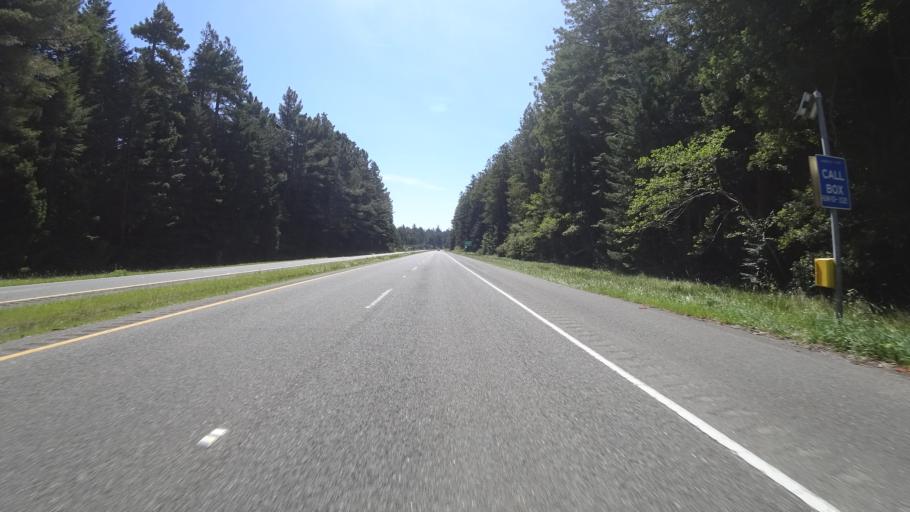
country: US
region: California
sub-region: Humboldt County
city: Westhaven-Moonstone
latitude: 41.0789
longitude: -124.1438
